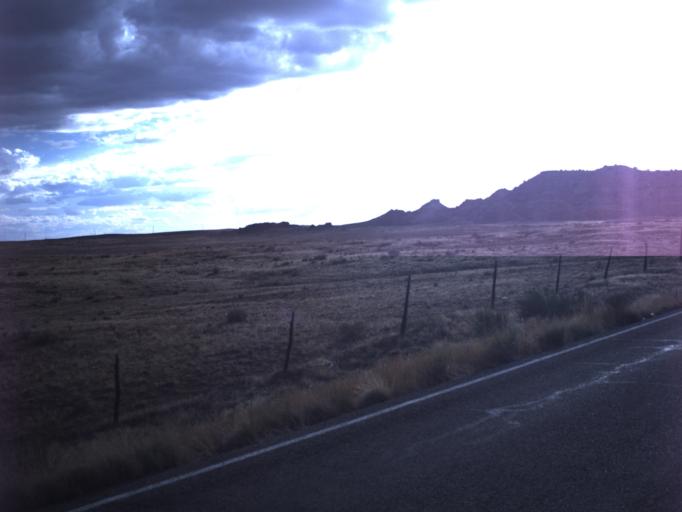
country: US
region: Utah
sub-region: San Juan County
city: Blanding
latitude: 37.4226
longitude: -109.4680
